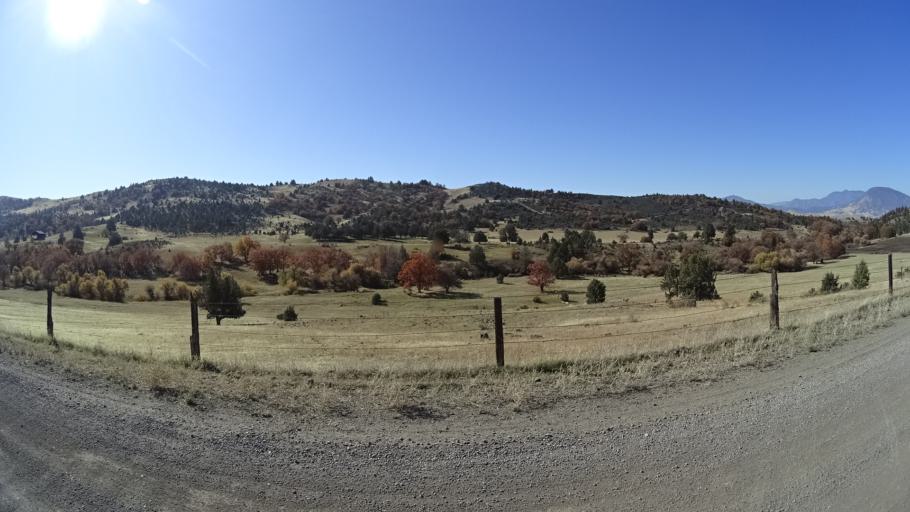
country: US
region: California
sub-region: Siskiyou County
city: Montague
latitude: 41.7984
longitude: -122.3673
